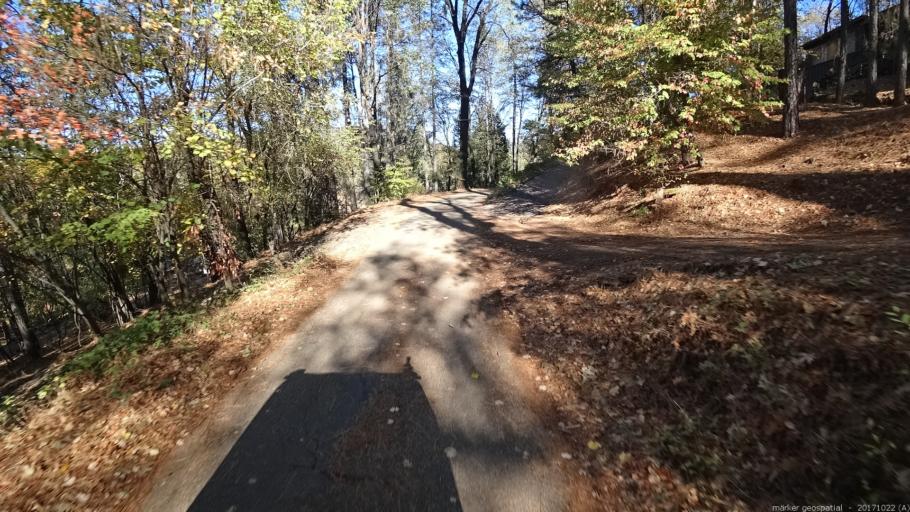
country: US
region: California
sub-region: Shasta County
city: Shasta Lake
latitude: 40.8404
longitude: -122.3601
